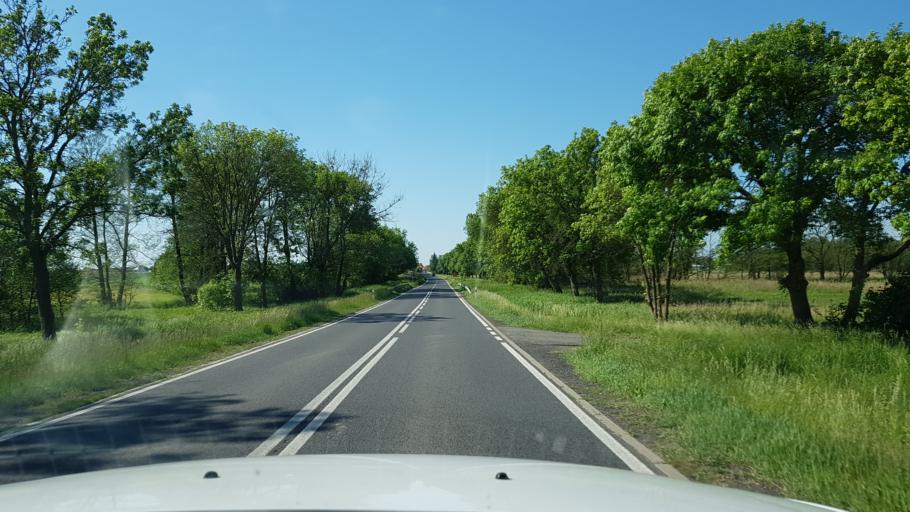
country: PL
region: West Pomeranian Voivodeship
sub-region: Powiat gryfinski
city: Mieszkowice
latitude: 52.7990
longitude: 14.4975
